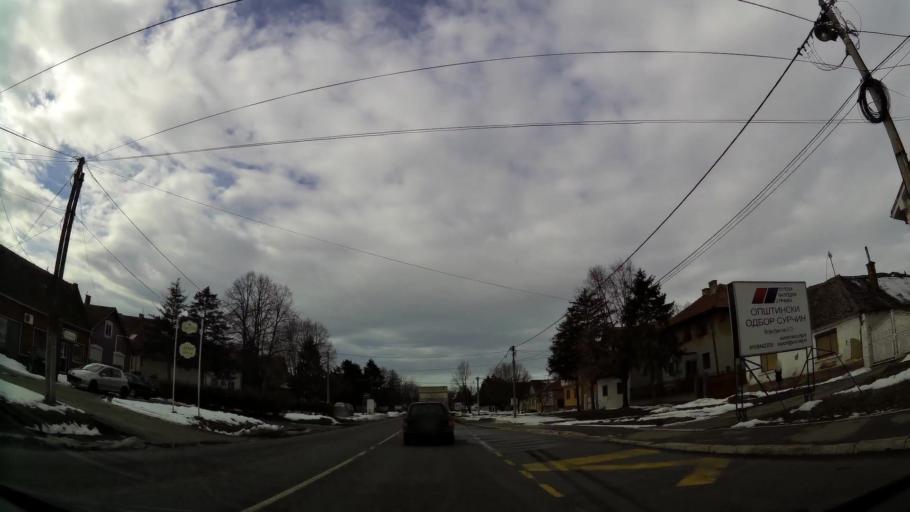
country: RS
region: Central Serbia
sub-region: Belgrade
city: Surcin
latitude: 44.7935
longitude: 20.2847
